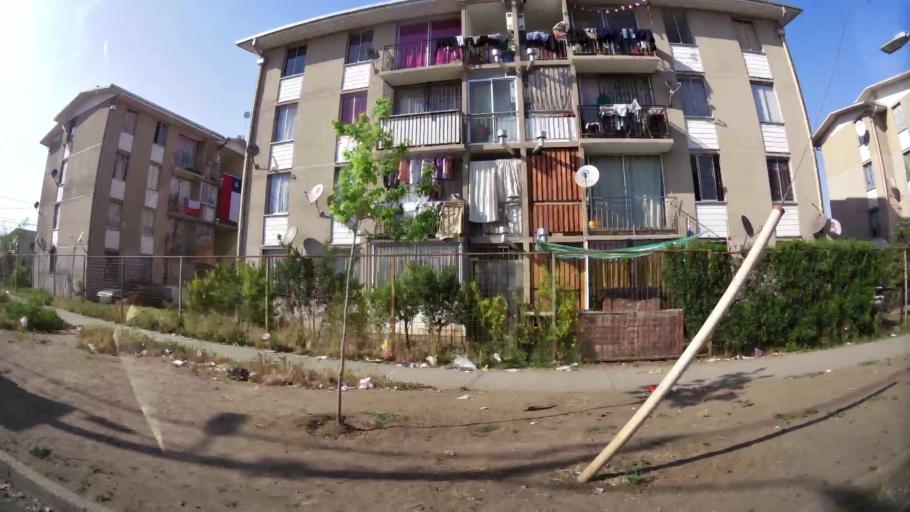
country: CL
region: Santiago Metropolitan
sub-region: Provincia de Santiago
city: Lo Prado
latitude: -33.4197
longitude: -70.7606
